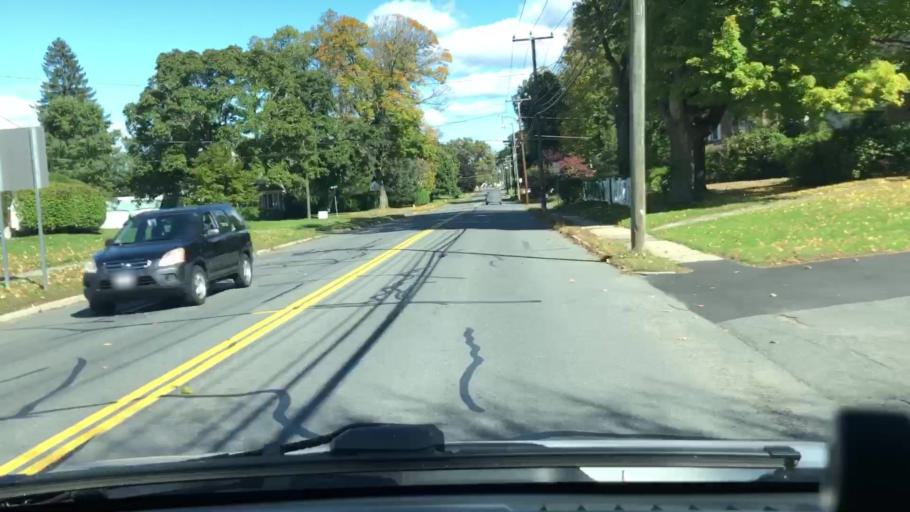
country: US
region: Massachusetts
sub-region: Franklin County
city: Greenfield
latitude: 42.5966
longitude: -72.5901
